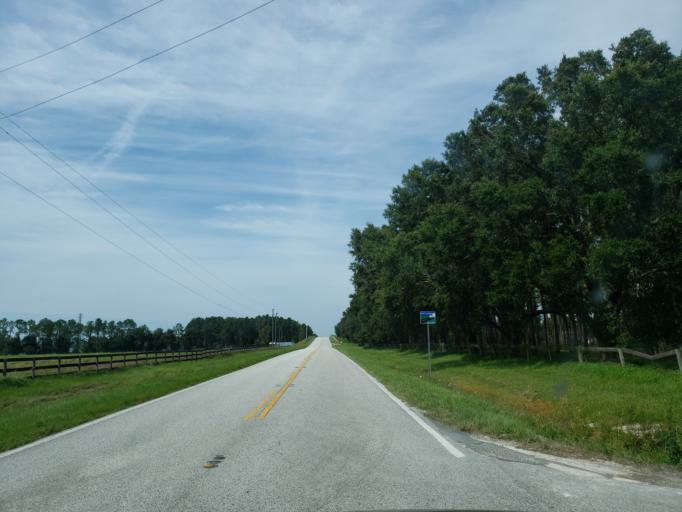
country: US
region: Florida
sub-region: Pasco County
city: San Antonio
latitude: 28.3980
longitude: -82.3118
